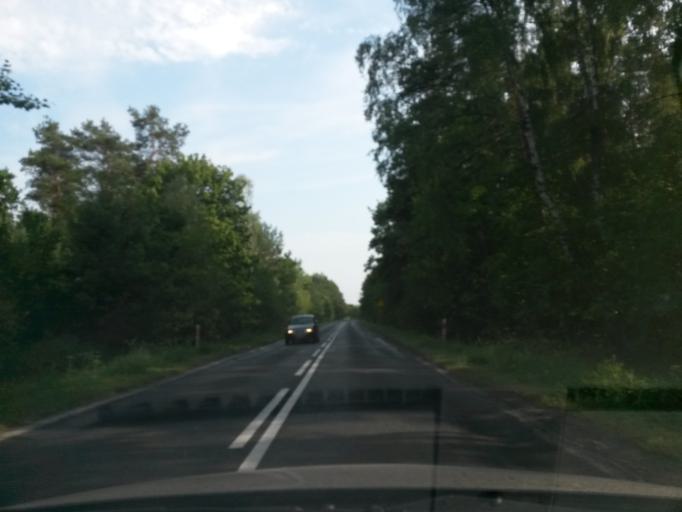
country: PL
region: Masovian Voivodeship
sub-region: Powiat sierpecki
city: Sierpc
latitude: 52.8928
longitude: 19.6512
